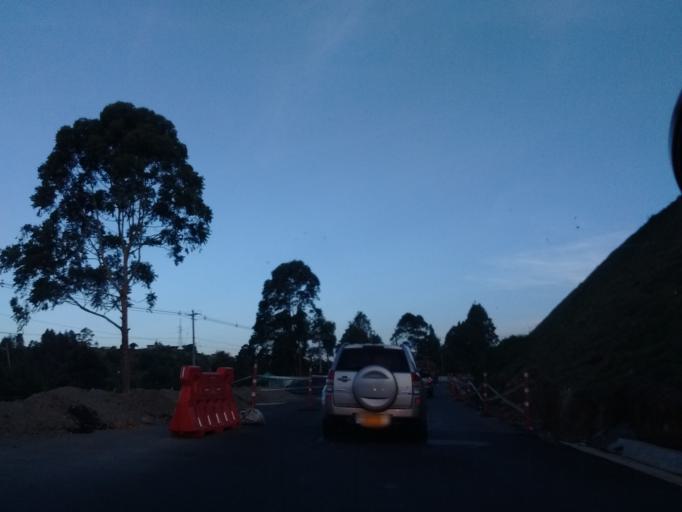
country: CO
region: Antioquia
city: Marinilla
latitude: 6.1656
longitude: -75.3201
